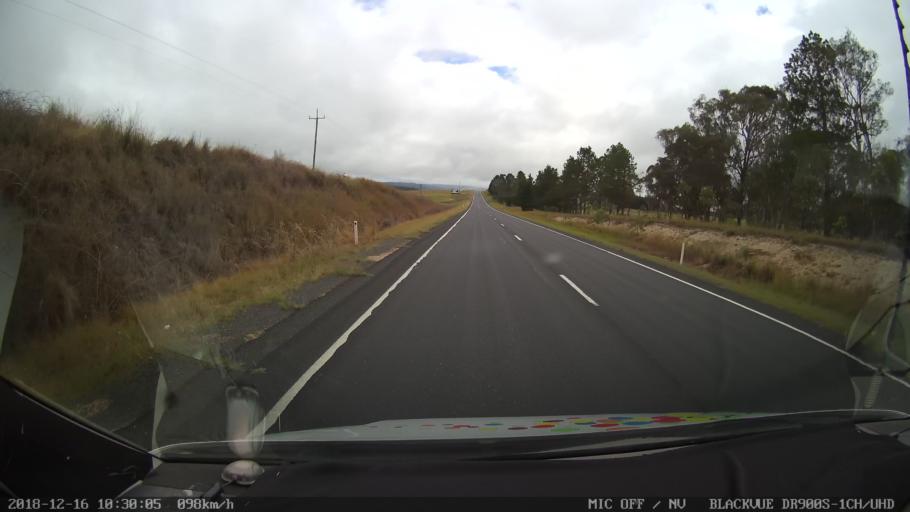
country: AU
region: New South Wales
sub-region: Tenterfield Municipality
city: Carrolls Creek
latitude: -29.0985
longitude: 152.0016
